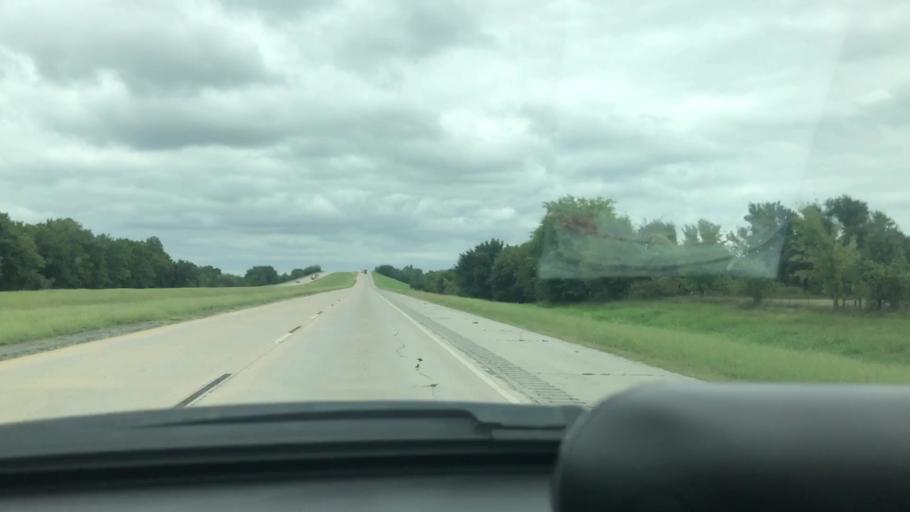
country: US
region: Oklahoma
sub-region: Wagoner County
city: Wagoner
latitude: 35.8768
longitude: -95.4025
